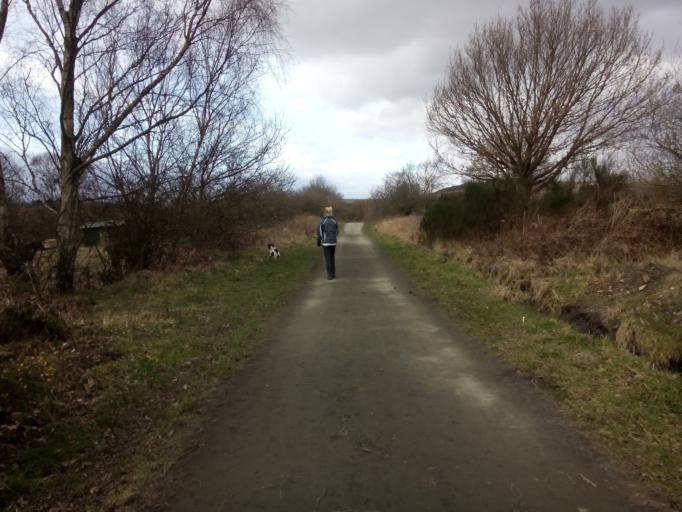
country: GB
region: England
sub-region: County Durham
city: Ushaw Moor
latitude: 54.7728
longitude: -1.6386
